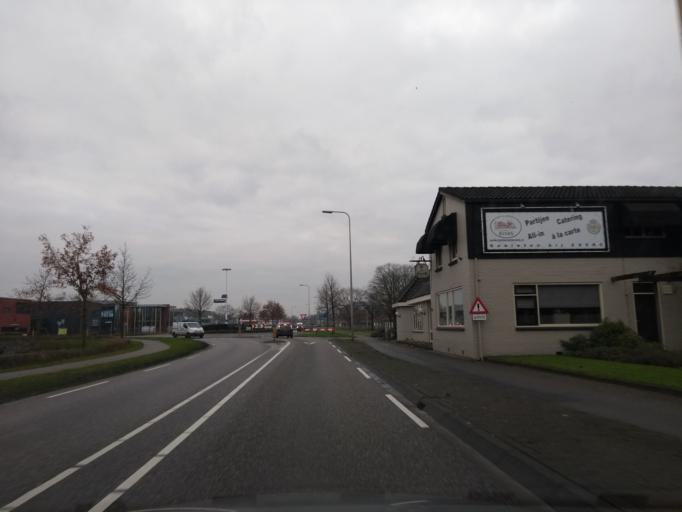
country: NL
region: Overijssel
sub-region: Gemeente Haaksbergen
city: Haaksbergen
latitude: 52.1743
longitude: 6.7404
